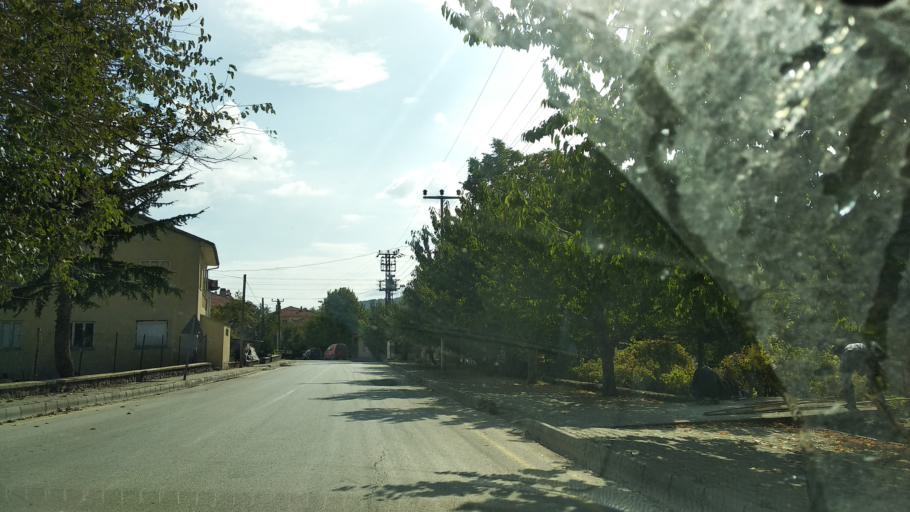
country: TR
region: Bolu
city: Seben
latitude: 40.4105
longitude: 31.5707
